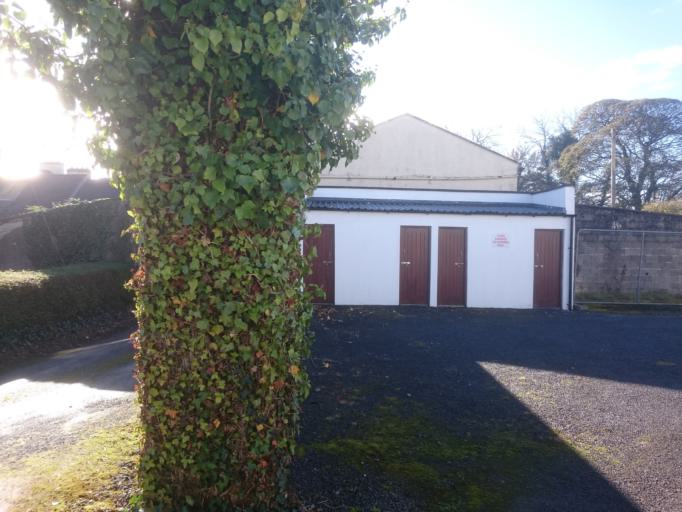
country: IE
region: Connaught
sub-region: Maigh Eo
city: Claremorris
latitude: 53.7222
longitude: -8.9982
